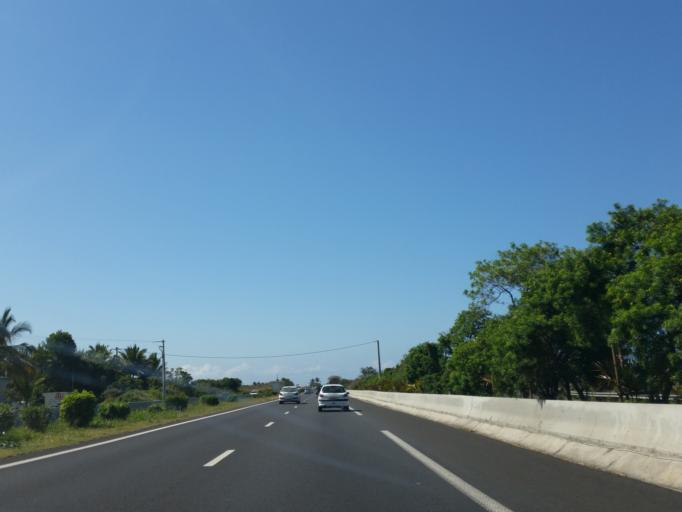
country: RE
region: Reunion
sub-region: Reunion
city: Saint-Louis
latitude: -21.3086
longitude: 55.4321
